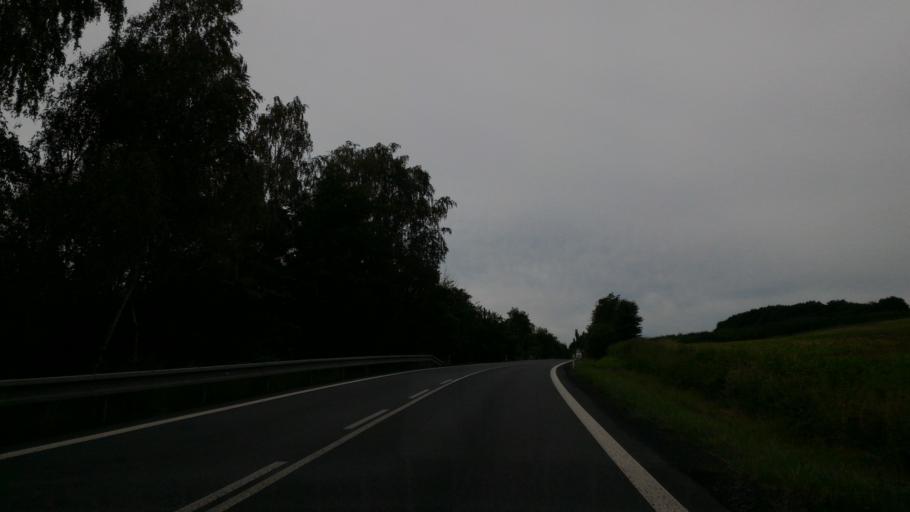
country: CZ
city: Duba
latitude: 50.6004
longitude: 14.5640
